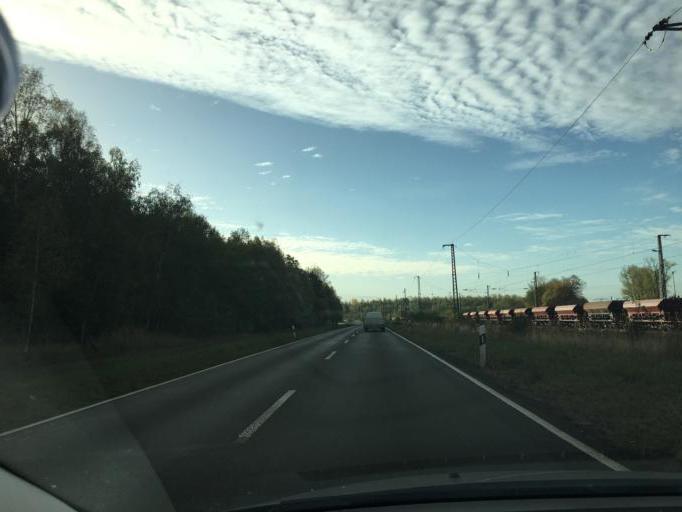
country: DE
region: Saxony
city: Neukieritzsch
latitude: 51.1446
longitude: 12.4171
